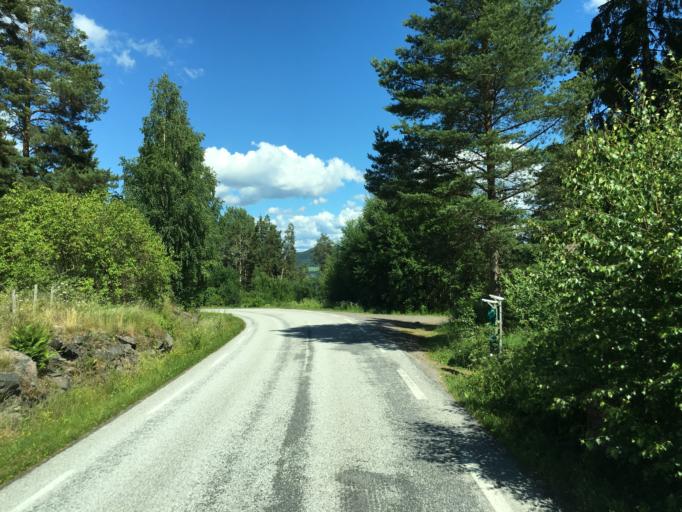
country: NO
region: Oppland
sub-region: Jevnaker
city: Jevnaker
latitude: 60.3376
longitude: 10.3555
